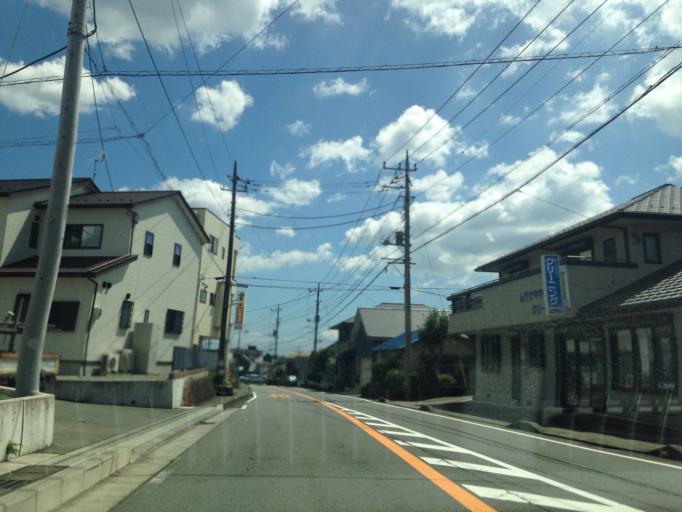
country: JP
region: Shizuoka
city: Mishima
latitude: 35.2002
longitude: 138.9065
